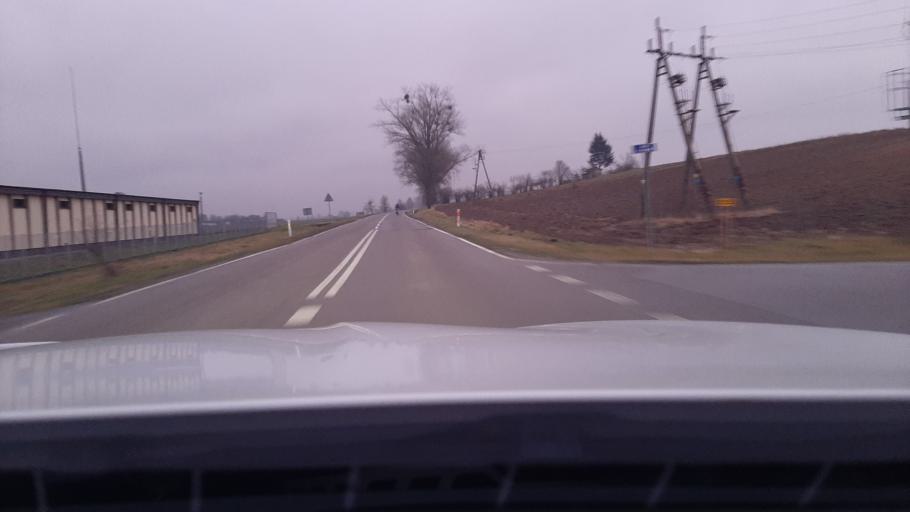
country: PL
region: Lublin Voivodeship
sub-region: Powiat lubelski
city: Garbow
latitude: 51.3477
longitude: 22.3723
